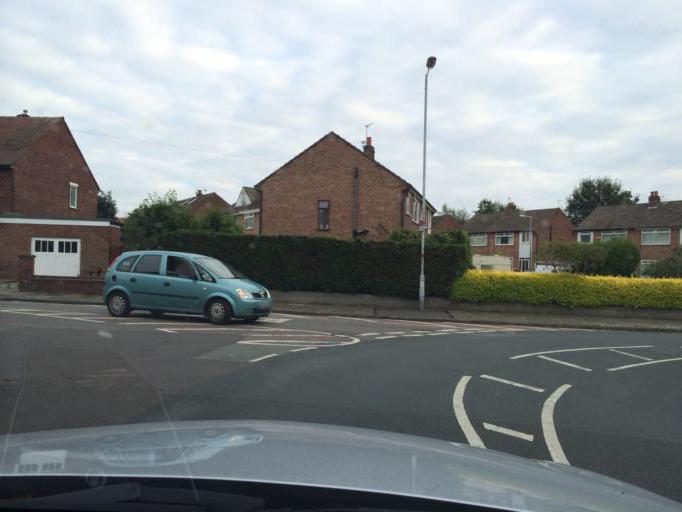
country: GB
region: England
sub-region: Borough of Stockport
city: Bredbury
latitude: 53.4038
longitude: -2.1288
